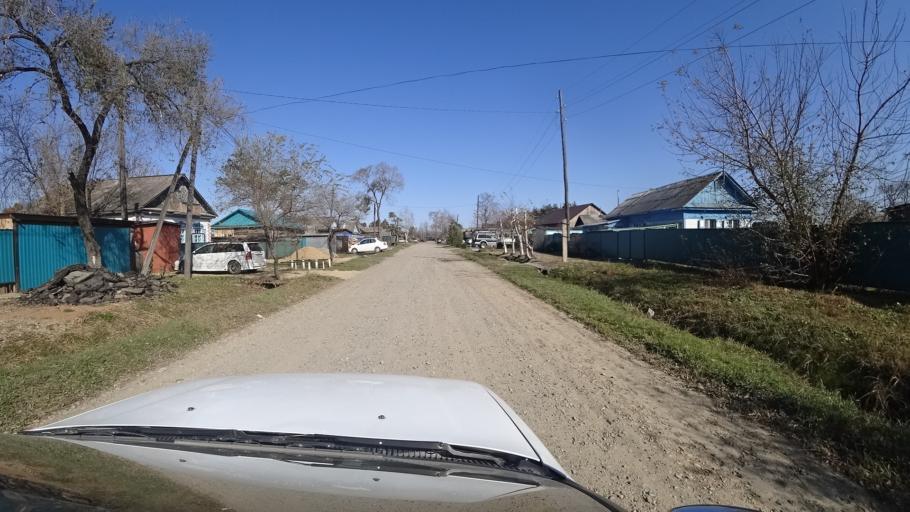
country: RU
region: Primorskiy
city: Dal'nerechensk
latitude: 45.9270
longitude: 133.7505
